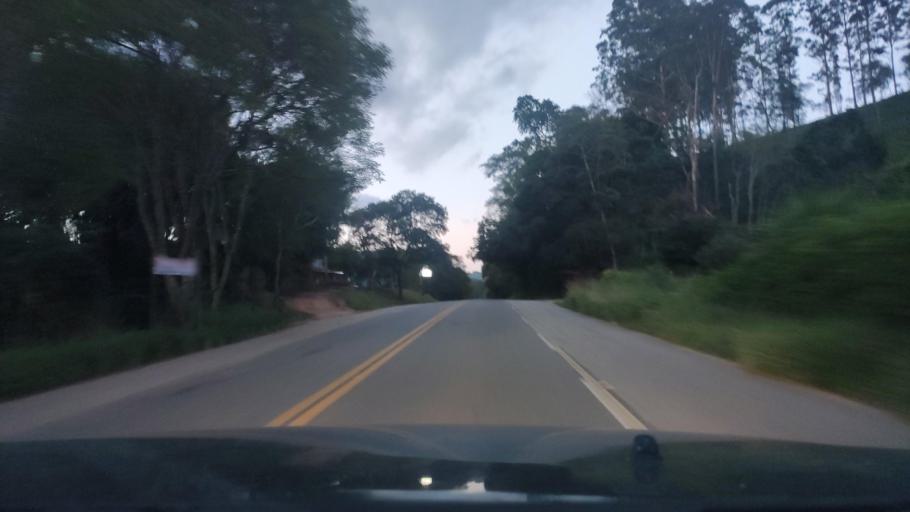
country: BR
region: Sao Paulo
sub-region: Campos Do Jordao
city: Campos do Jordao
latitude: -22.7632
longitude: -45.7403
